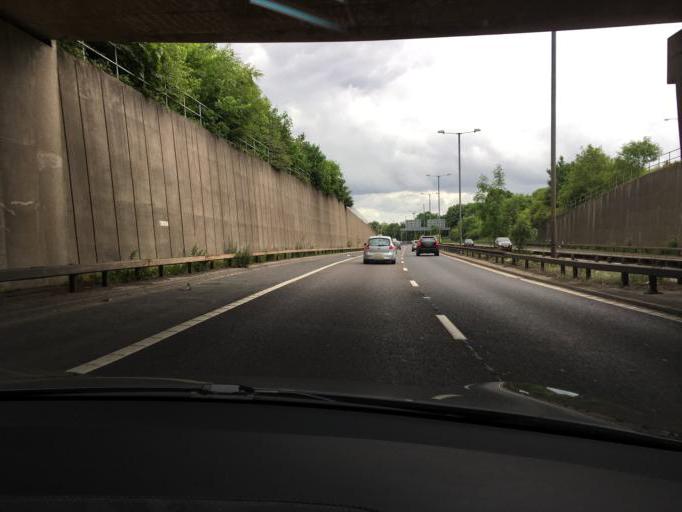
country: GB
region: England
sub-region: Manchester
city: Didsbury
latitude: 53.3965
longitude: -2.2565
